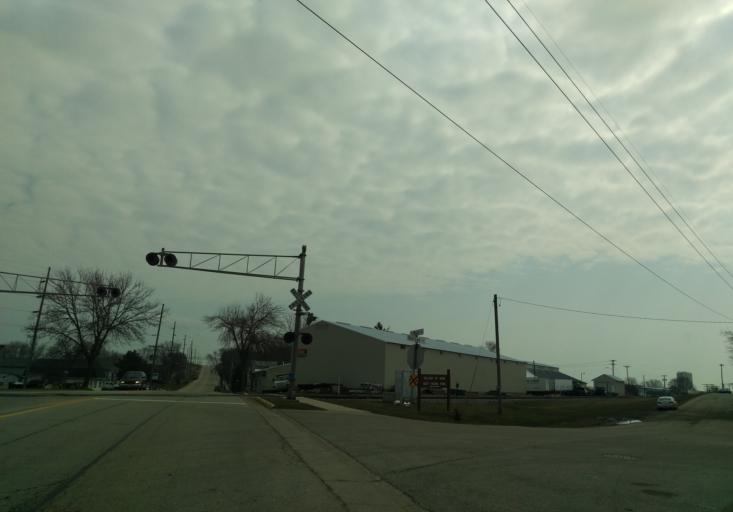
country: US
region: Wisconsin
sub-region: Columbia County
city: Lodi
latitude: 43.2504
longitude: -89.4995
